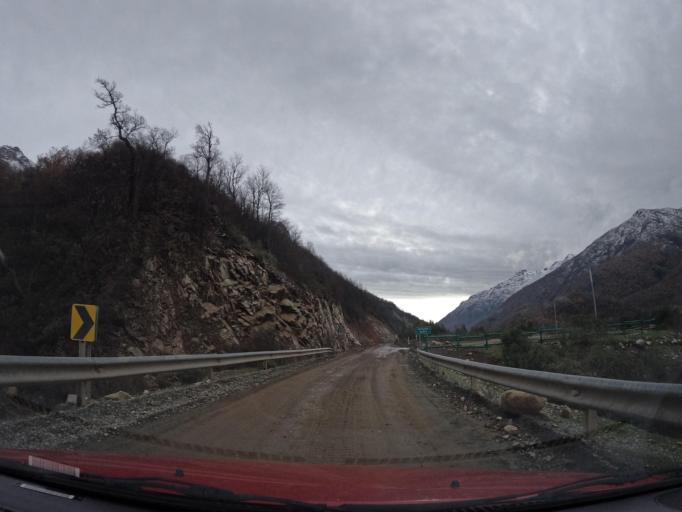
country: CL
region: Maule
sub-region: Provincia de Linares
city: Colbun
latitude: -35.8584
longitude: -71.1500
